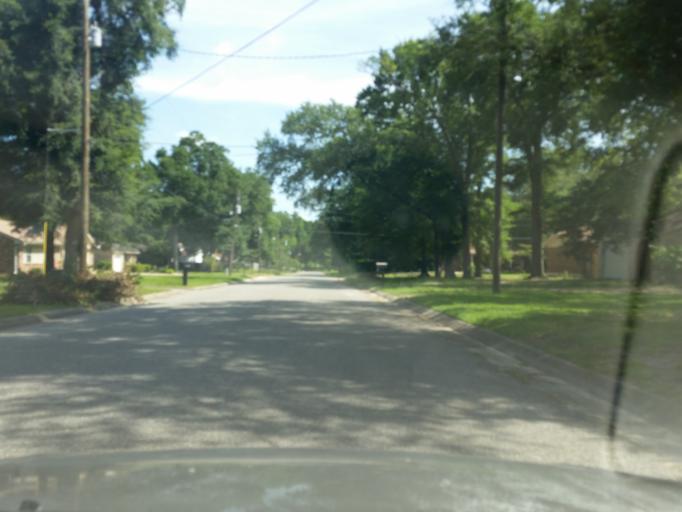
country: US
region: Florida
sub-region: Escambia County
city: Ferry Pass
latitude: 30.5138
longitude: -87.1926
